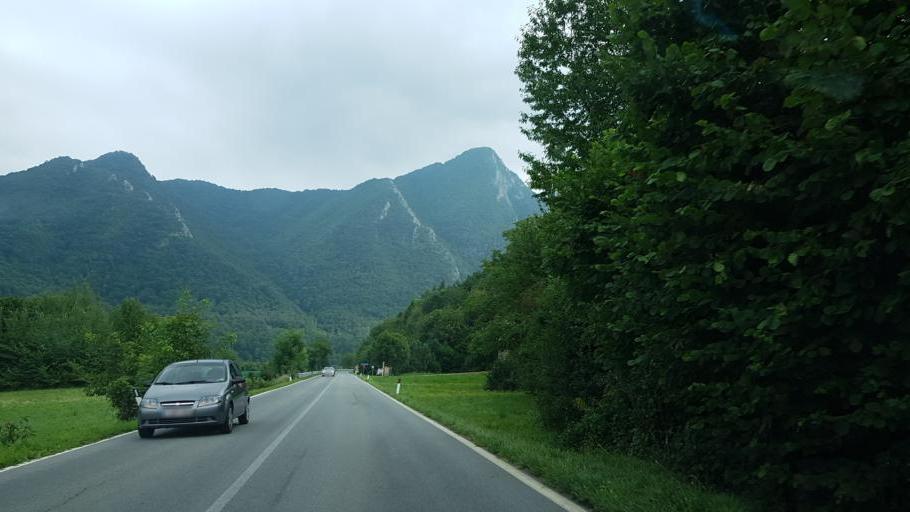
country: IT
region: Piedmont
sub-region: Provincia di Cuneo
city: Moiola
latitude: 44.3295
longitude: 7.3957
